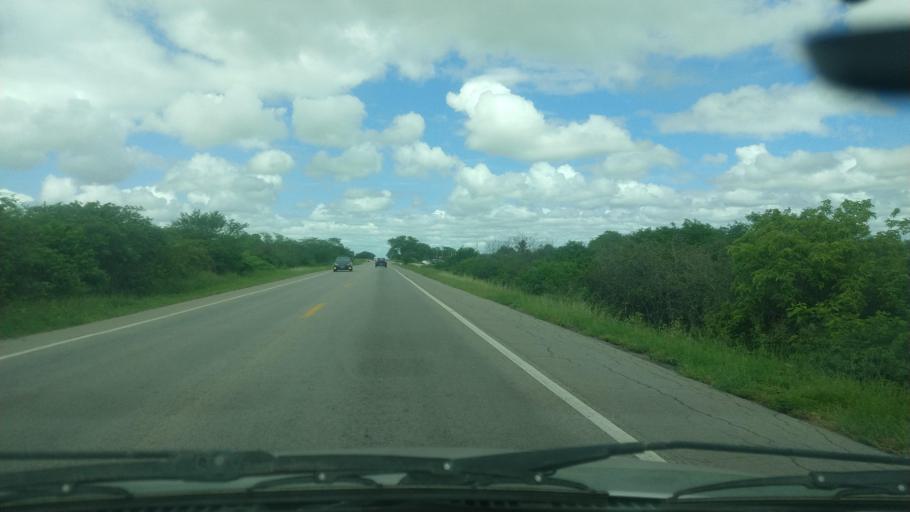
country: BR
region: Rio Grande do Norte
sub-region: Tangara
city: Tangara
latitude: -6.1677
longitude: -35.7594
